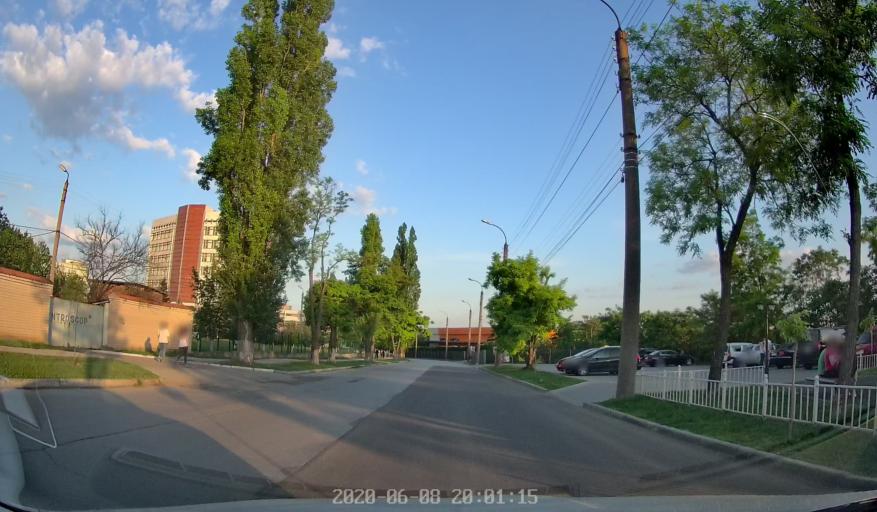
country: MD
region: Chisinau
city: Chisinau
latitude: 47.0133
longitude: 28.8836
